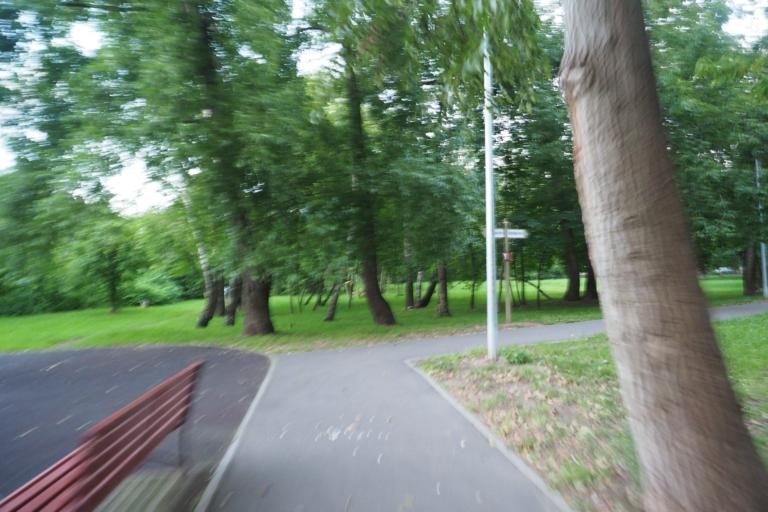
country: RU
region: Moscow
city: Kotlovka
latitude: 55.6821
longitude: 37.6068
